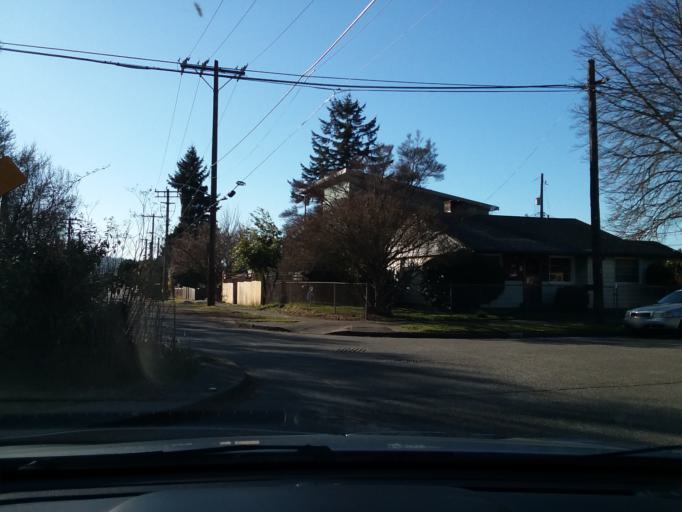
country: US
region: Washington
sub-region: King County
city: Seattle
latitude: 47.6630
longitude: -122.3639
